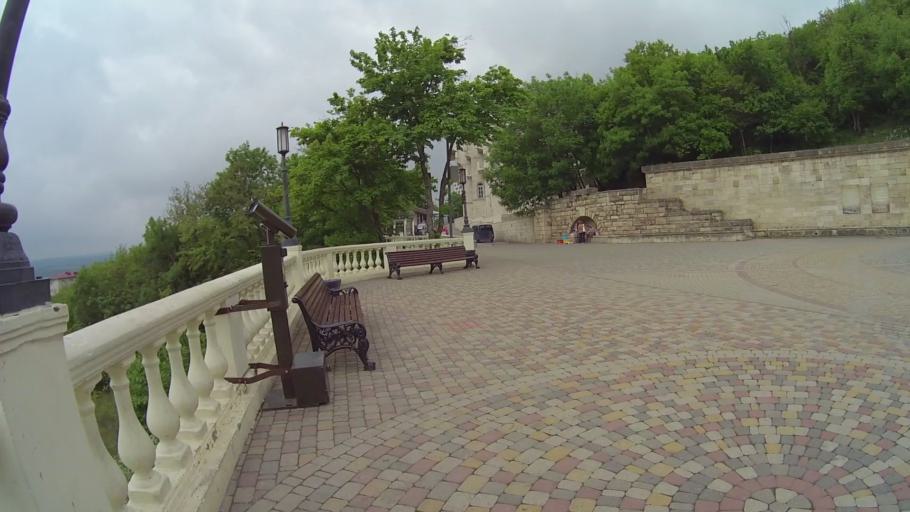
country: RU
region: Stavropol'skiy
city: Goryachevodskiy
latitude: 44.0463
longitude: 43.0997
